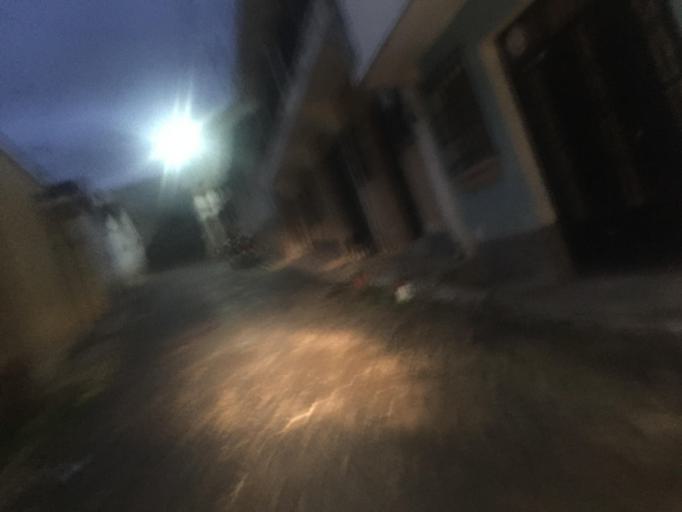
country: GT
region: Totonicapan
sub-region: Municipio de Totonicapan
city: Totonicapan
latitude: 14.9159
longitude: -91.3591
